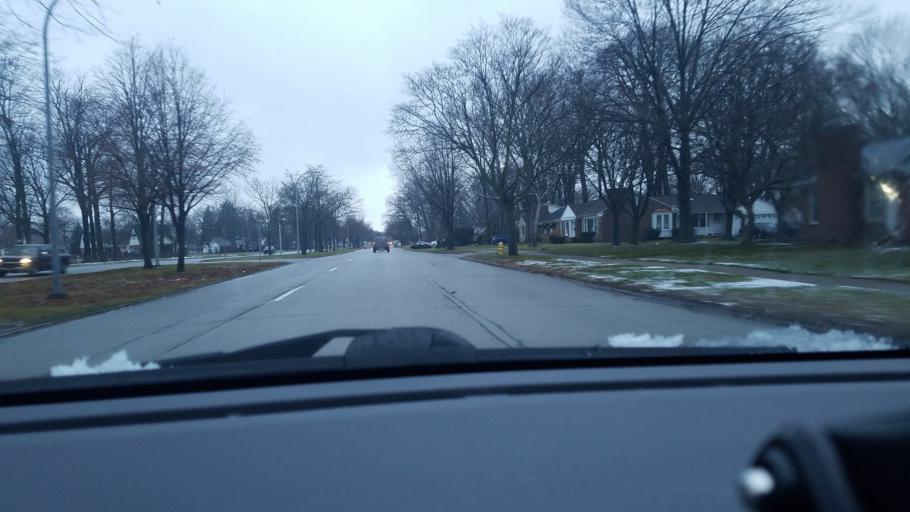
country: US
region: Michigan
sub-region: Wayne County
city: Allen Park
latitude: 42.2873
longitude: -83.2383
